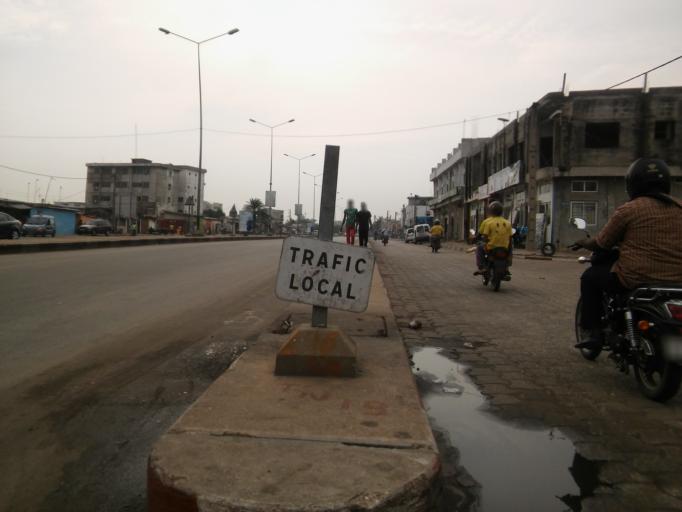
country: BJ
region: Littoral
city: Cotonou
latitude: 6.3707
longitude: 2.4105
